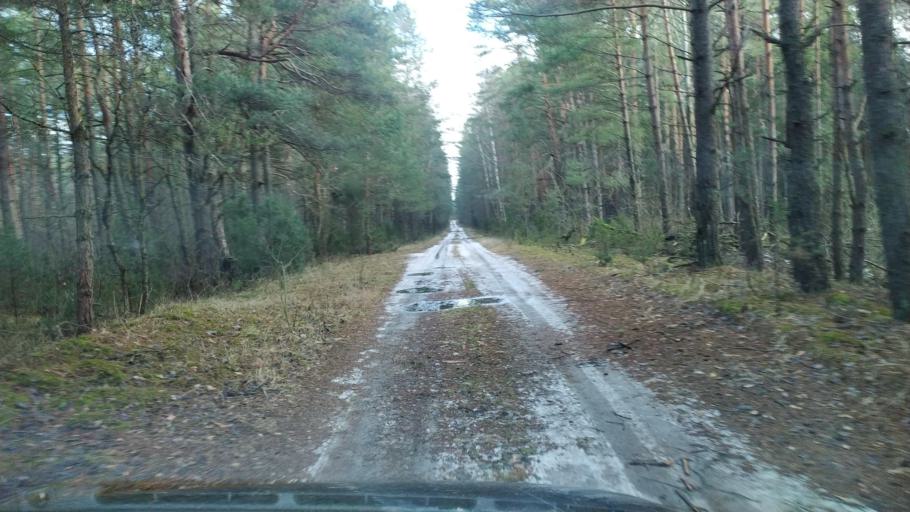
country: BY
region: Brest
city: Kamyanyets
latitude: 52.4280
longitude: 23.9957
